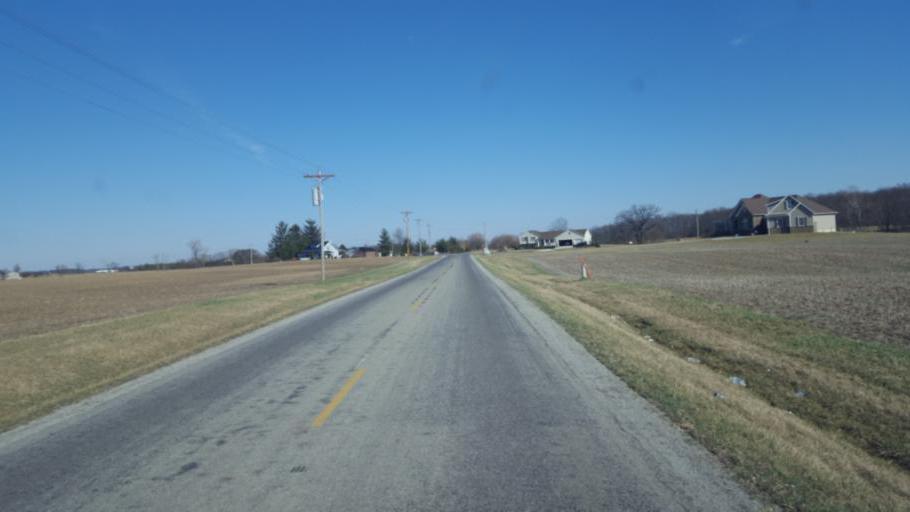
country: US
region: Ohio
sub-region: Union County
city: Richwood
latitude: 40.5466
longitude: -83.4409
